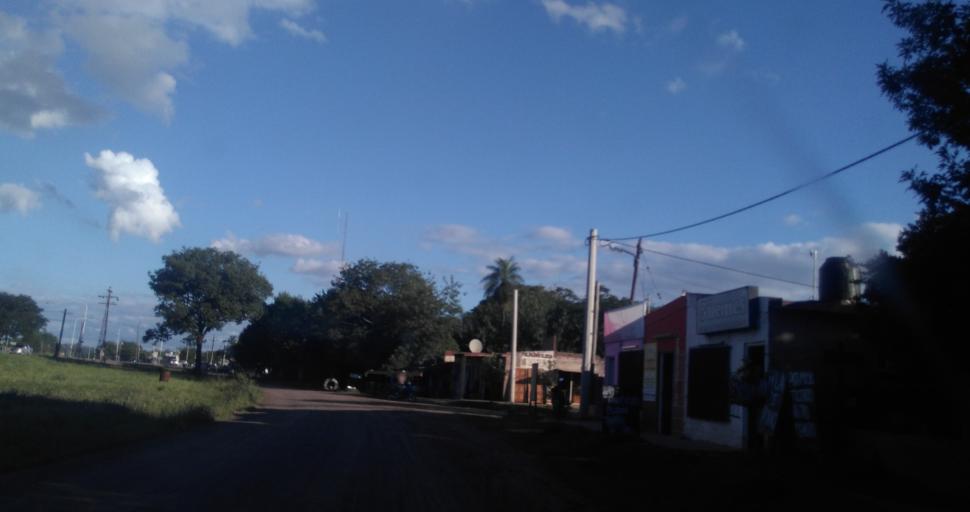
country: AR
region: Chaco
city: Fontana
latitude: -27.4222
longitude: -59.0343
